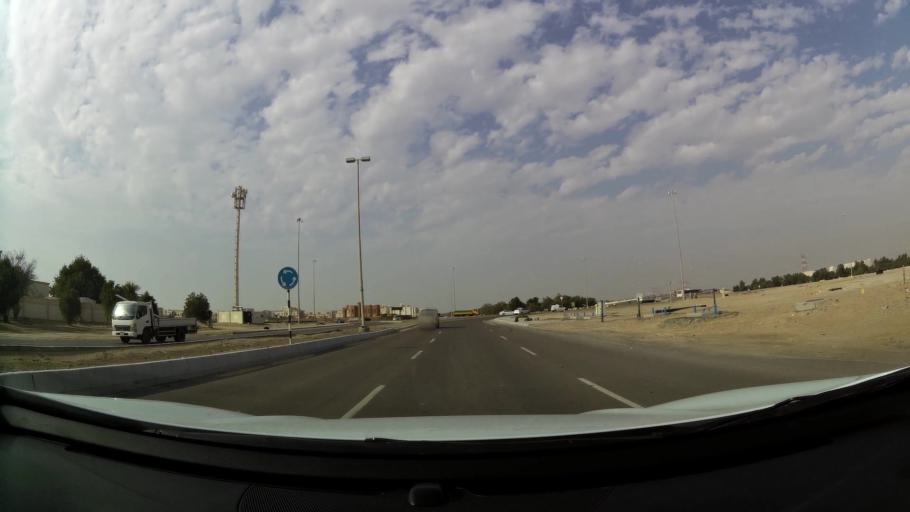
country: AE
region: Abu Dhabi
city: Abu Dhabi
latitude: 24.3472
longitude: 54.5662
